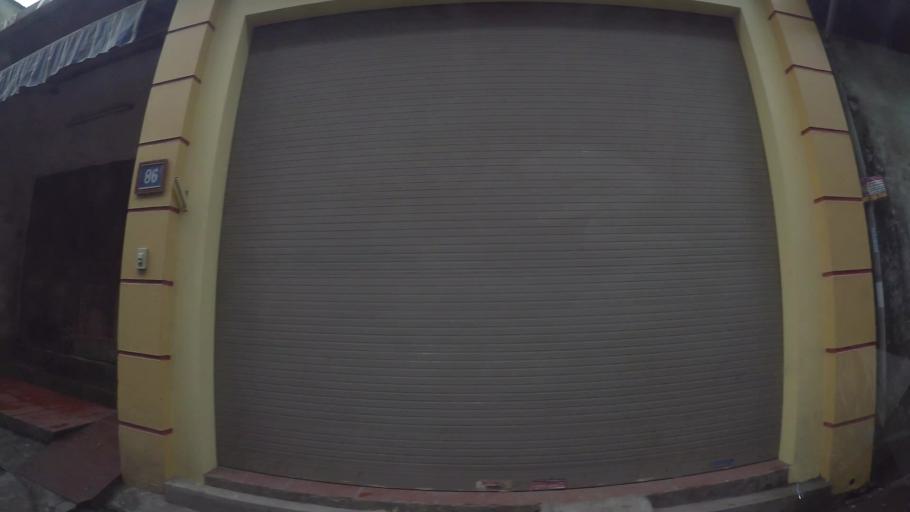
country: VN
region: Ha Noi
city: Van Dien
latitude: 20.9718
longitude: 105.8688
